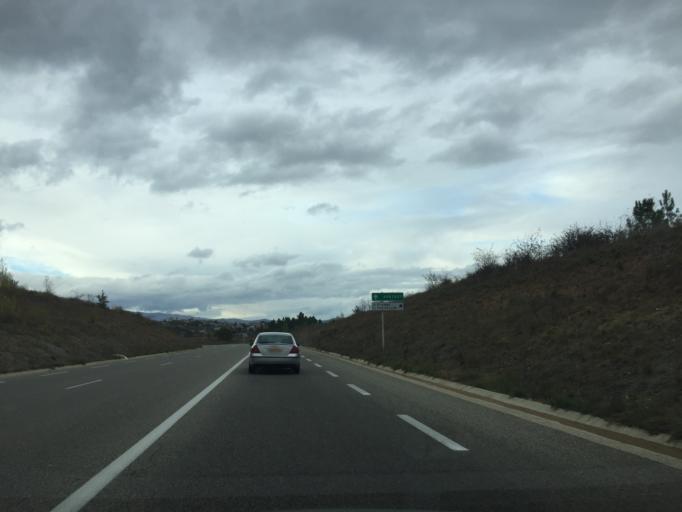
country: FR
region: Rhone-Alpes
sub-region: Departement de l'Ardeche
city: Saint-Etienne-de-Fontbellon
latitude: 44.5880
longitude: 4.3857
